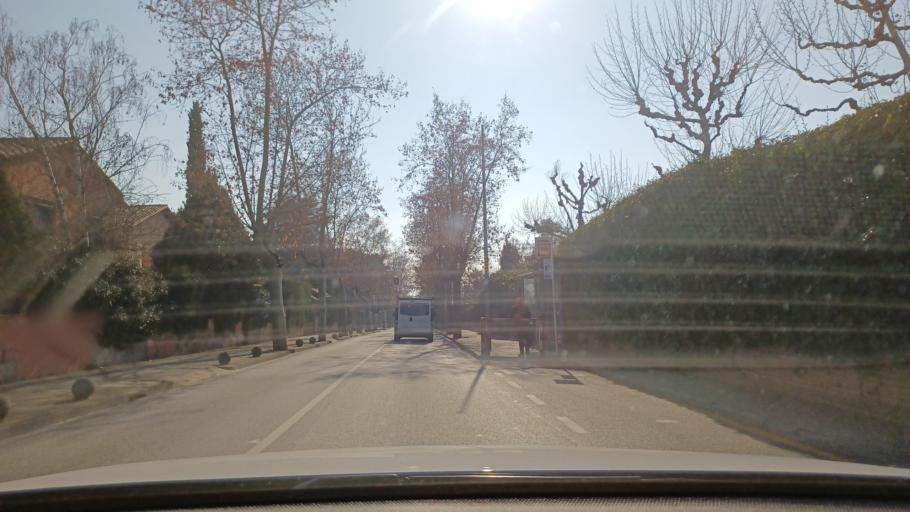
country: ES
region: Catalonia
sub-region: Provincia de Barcelona
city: L'Ametlla del Valles
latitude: 41.6657
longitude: 2.2658
